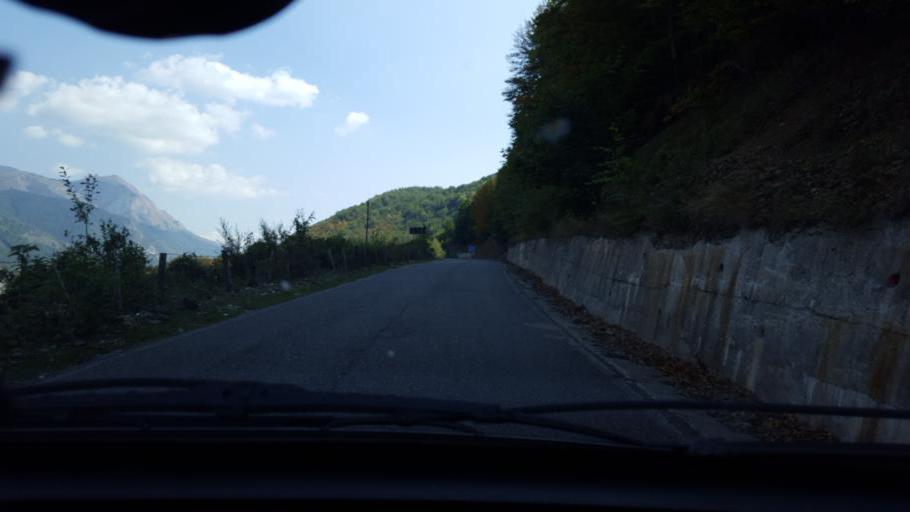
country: ME
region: Andrijevica
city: Andrijevica
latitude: 42.5799
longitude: 19.7405
